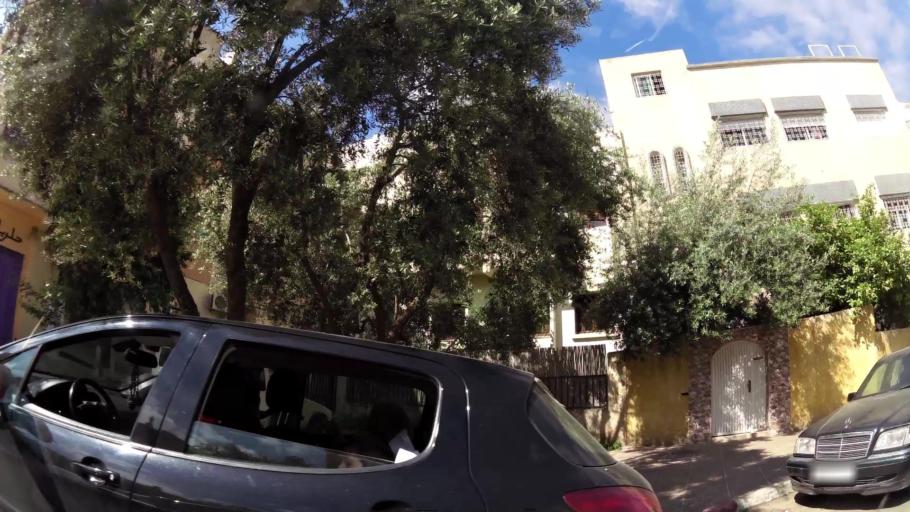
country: MA
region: Fes-Boulemane
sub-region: Fes
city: Fes
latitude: 34.0326
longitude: -5.0244
